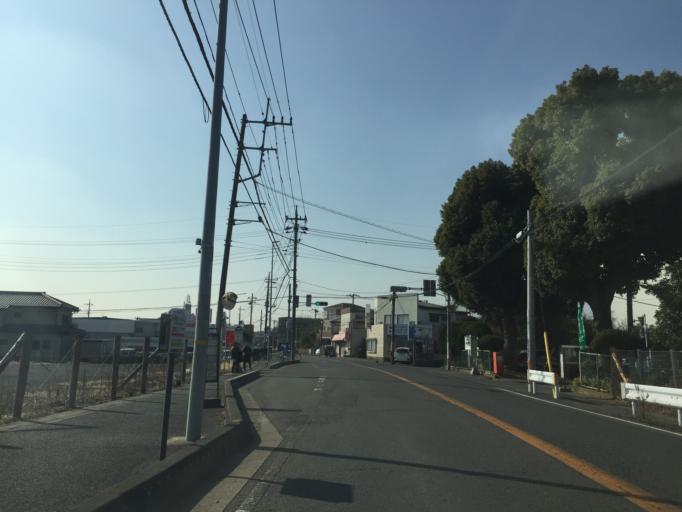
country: JP
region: Saitama
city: Shiki
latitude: 35.8419
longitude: 139.5834
